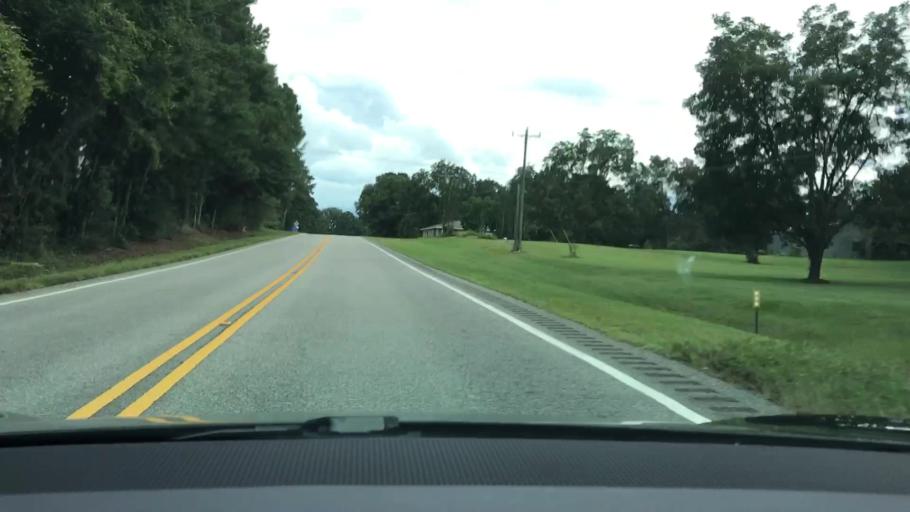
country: US
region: Alabama
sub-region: Coffee County
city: Elba
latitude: 31.5928
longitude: -86.0045
